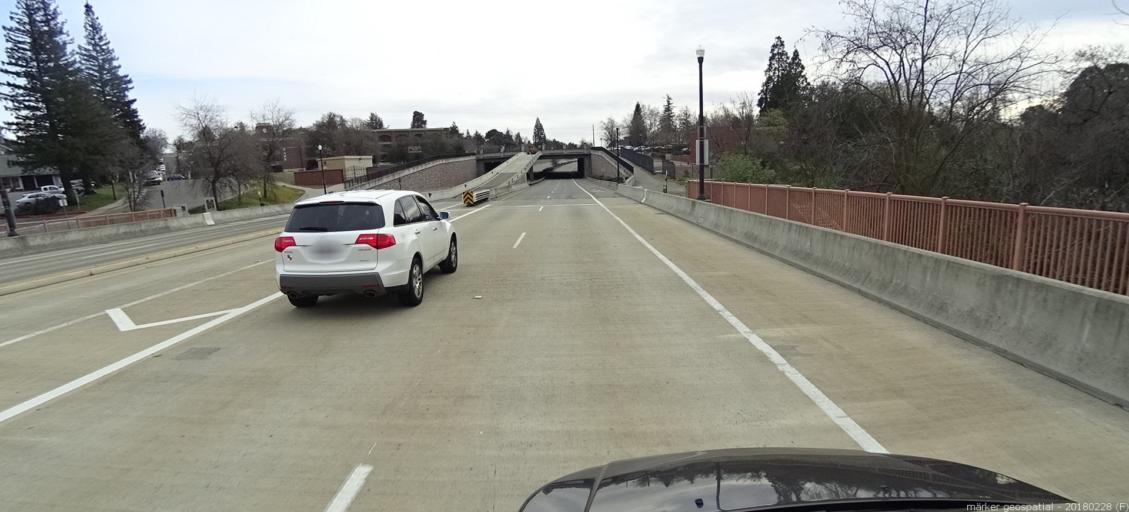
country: US
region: California
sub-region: Sacramento County
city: Folsom
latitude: 38.6785
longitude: -121.1809
